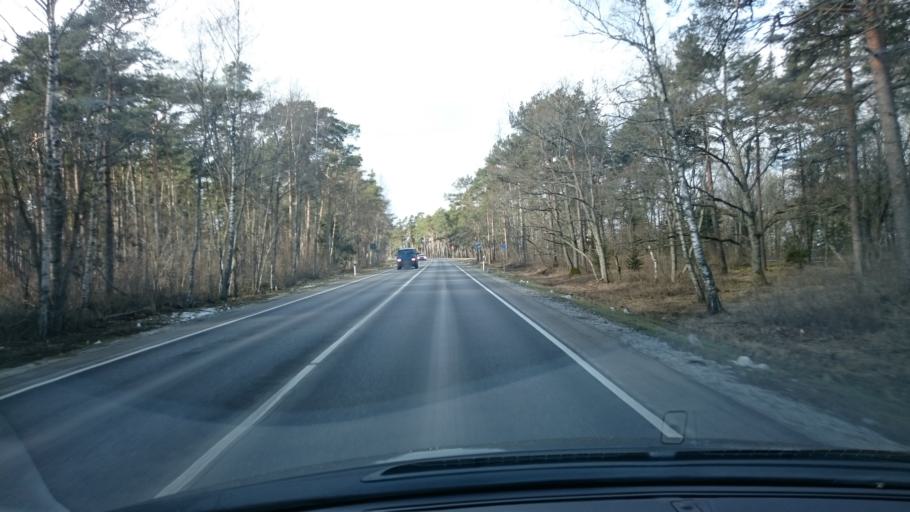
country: EE
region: Harju
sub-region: Keila linn
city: Keila
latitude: 59.3979
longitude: 24.2605
